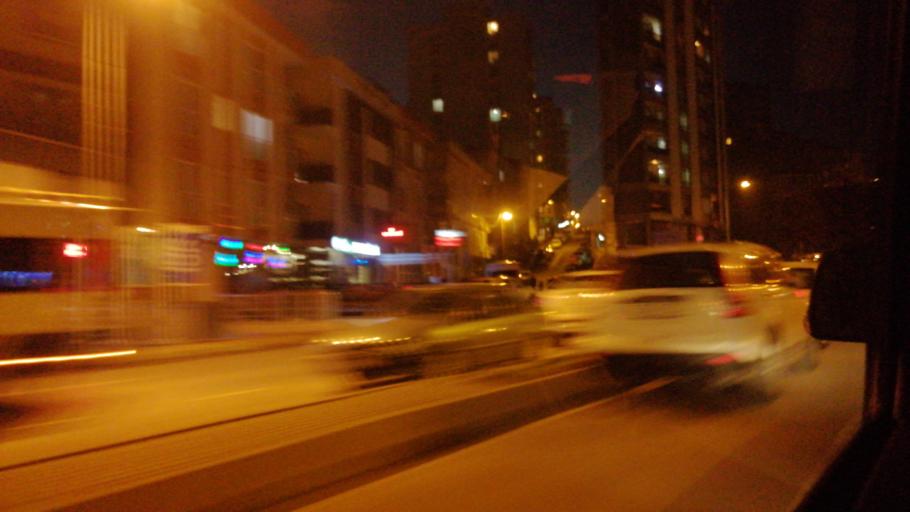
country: TR
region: Istanbul
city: Umraniye
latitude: 41.0074
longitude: 29.1287
